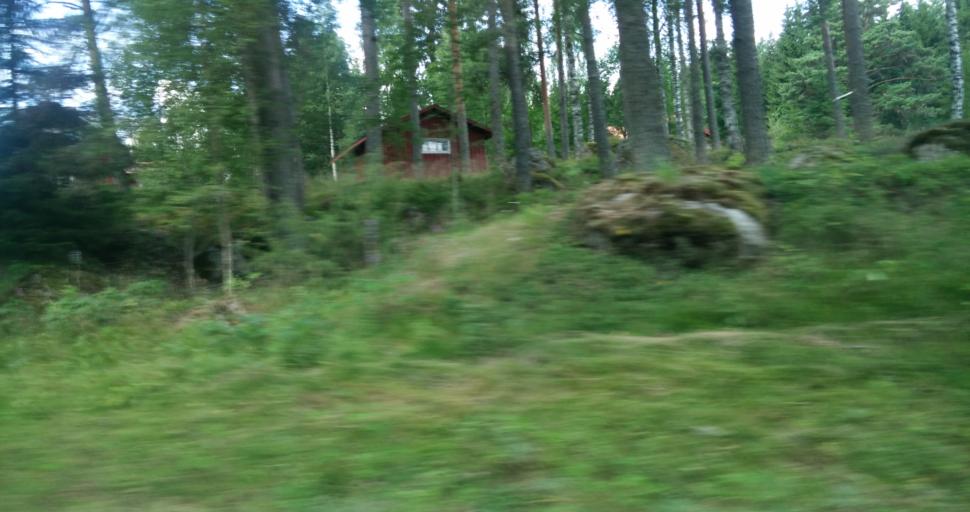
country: SE
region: Vaermland
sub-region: Hagfors Kommun
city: Ekshaerad
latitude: 60.1142
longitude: 13.4501
